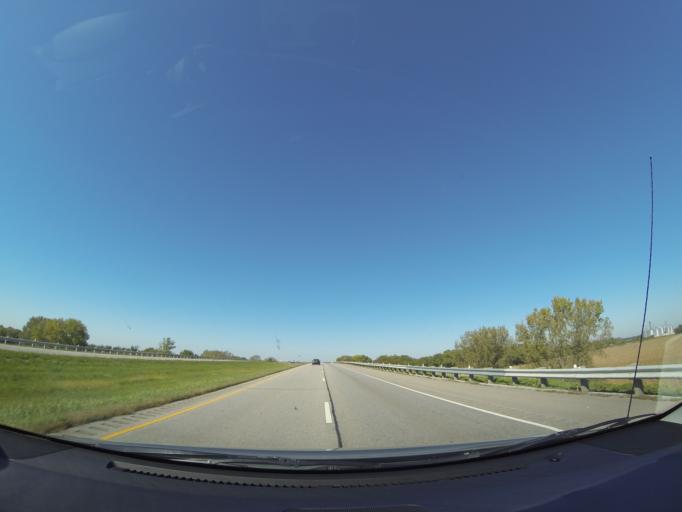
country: US
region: Nebraska
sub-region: Seward County
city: Milford
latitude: 40.8222
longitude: -97.0708
